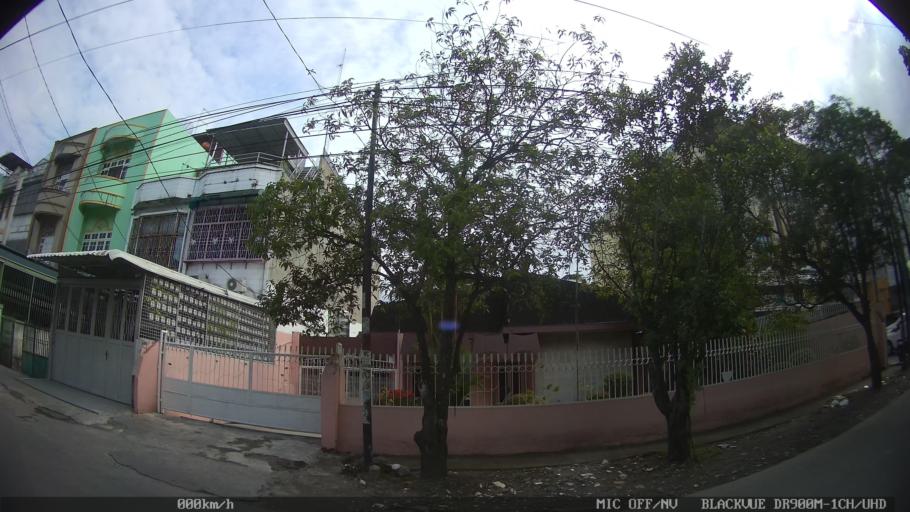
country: ID
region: North Sumatra
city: Medan
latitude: 3.6071
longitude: 98.6792
